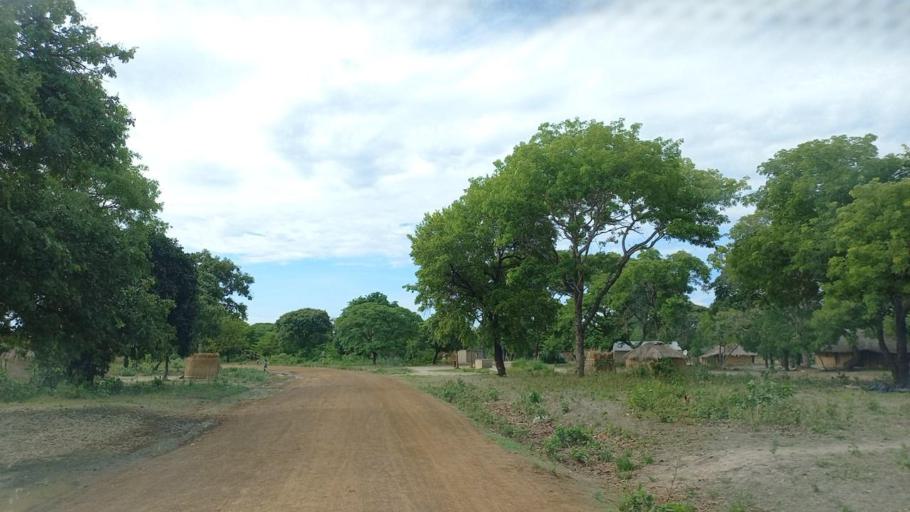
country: ZM
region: North-Western
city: Kabompo
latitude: -13.4602
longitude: 24.4270
